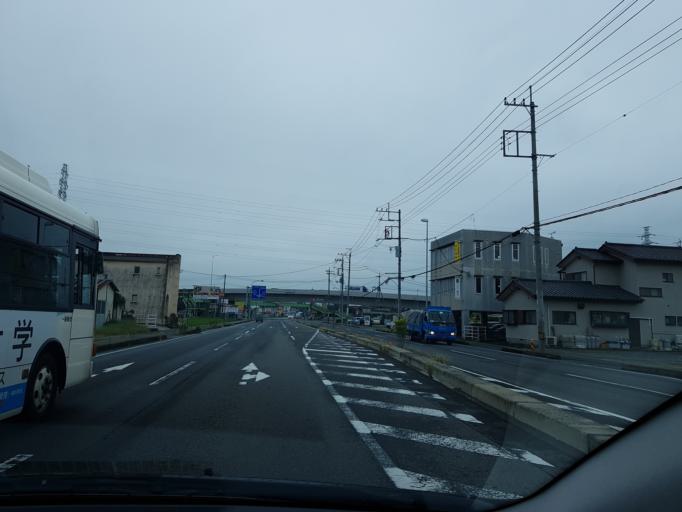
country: JP
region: Tochigi
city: Utsunomiya-shi
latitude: 36.5953
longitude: 139.8962
